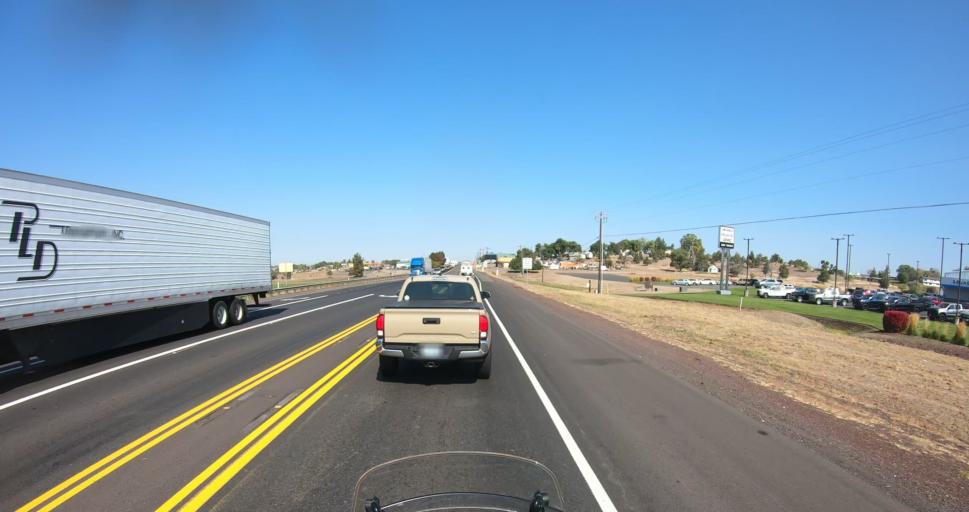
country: US
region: Oregon
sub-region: Jefferson County
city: Madras
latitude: 44.6064
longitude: -121.1408
